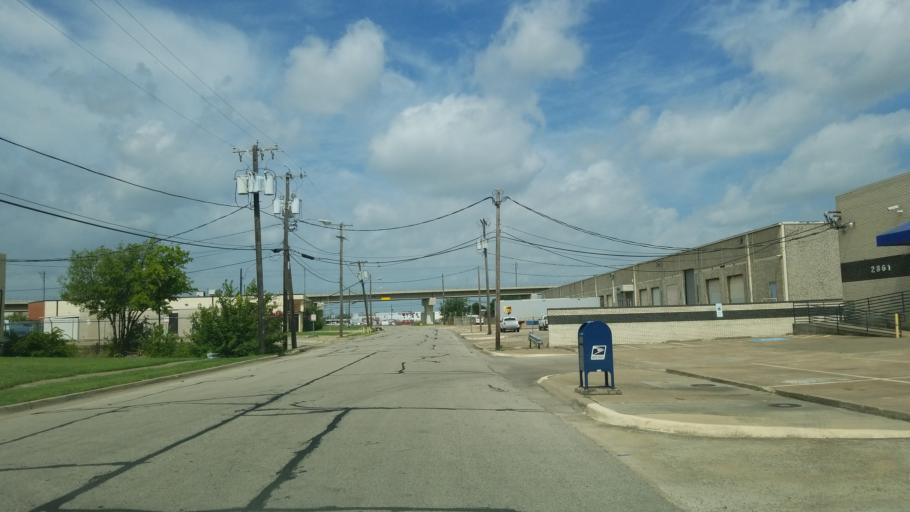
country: US
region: Texas
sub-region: Dallas County
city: Farmers Branch
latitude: 32.8780
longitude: -96.8808
